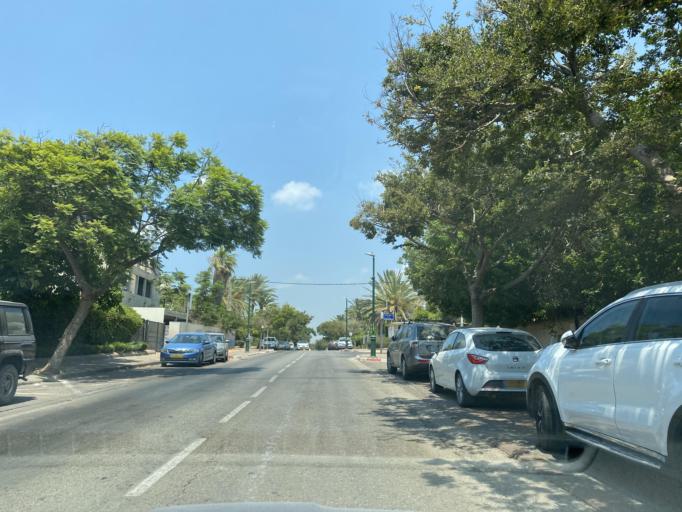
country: IL
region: Tel Aviv
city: Herzliya Pituah
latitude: 32.1762
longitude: 34.8046
